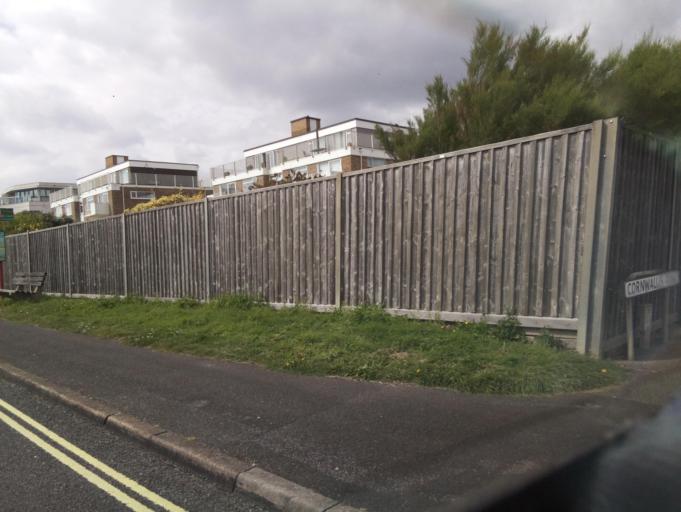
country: GB
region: England
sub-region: Hampshire
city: Milford on Sea
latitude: 50.7249
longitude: -1.6053
